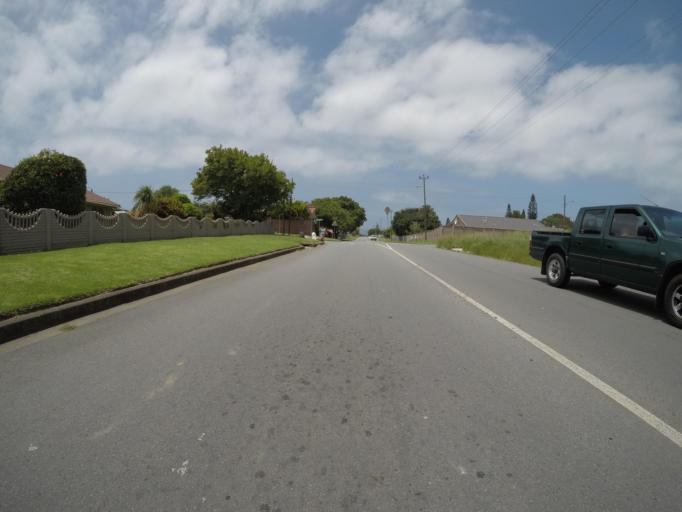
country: ZA
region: Eastern Cape
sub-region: Buffalo City Metropolitan Municipality
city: East London
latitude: -32.9449
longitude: 28.0116
